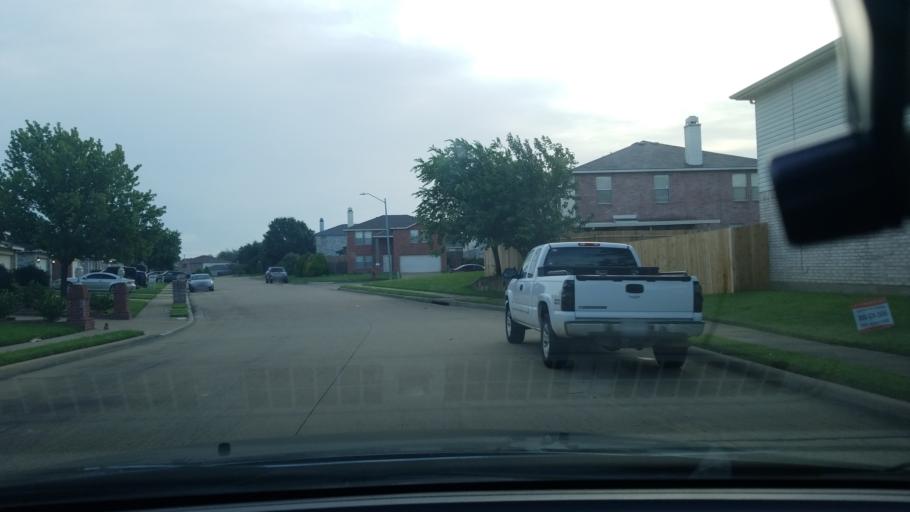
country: US
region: Texas
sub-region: Dallas County
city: Balch Springs
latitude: 32.7653
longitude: -96.6457
